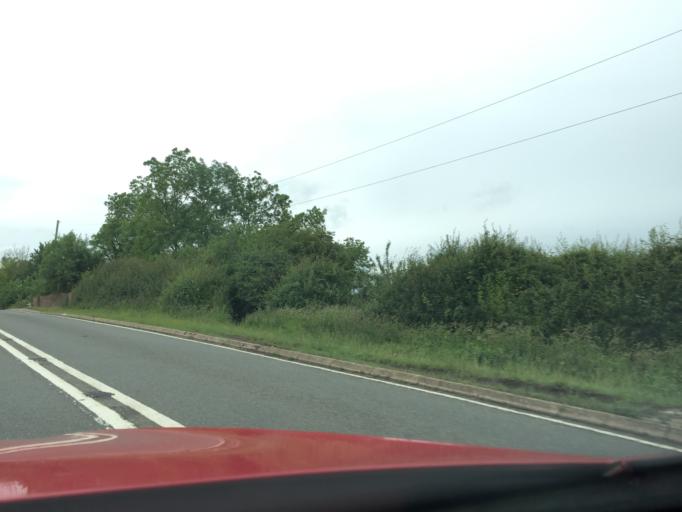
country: GB
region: England
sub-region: Warwickshire
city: Dunchurch
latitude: 52.2591
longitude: -1.3017
